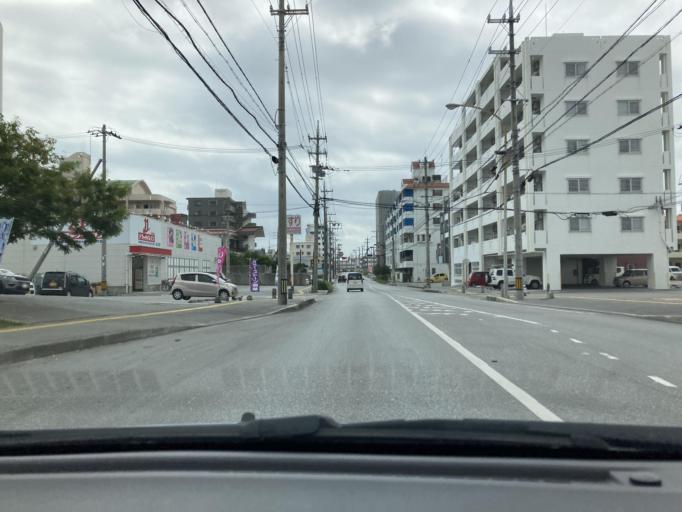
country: JP
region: Okinawa
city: Ginowan
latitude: 26.2520
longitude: 127.7725
